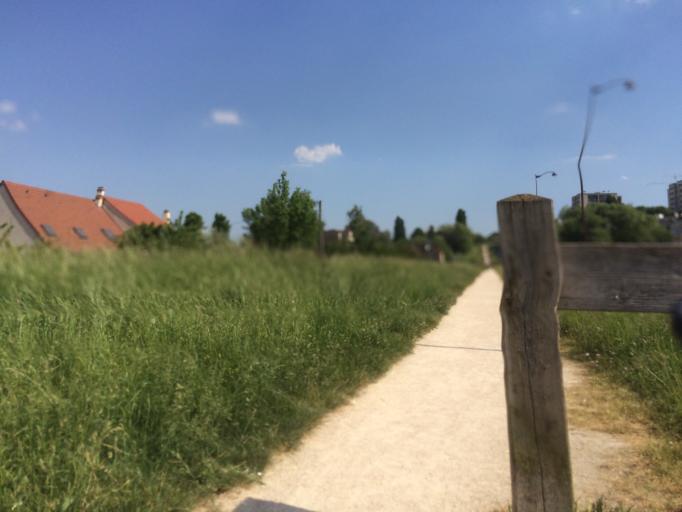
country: FR
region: Ile-de-France
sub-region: Departement de l'Essonne
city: Savigny-sur-Orge
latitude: 48.6757
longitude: 2.3636
